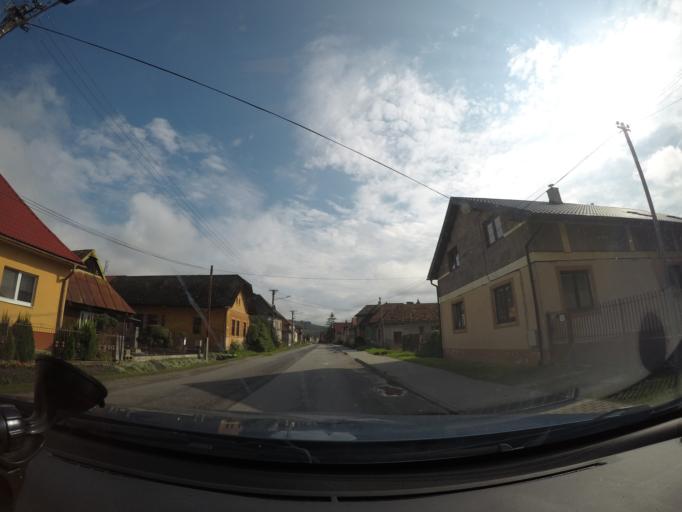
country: SK
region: Zilinsky
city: Ruzomberok
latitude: 49.0897
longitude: 19.3540
